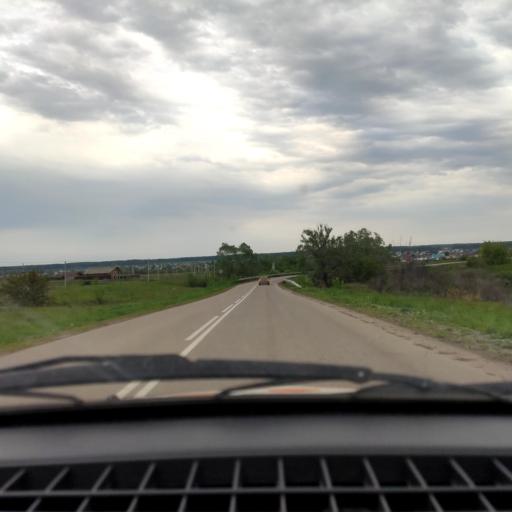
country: RU
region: Bashkortostan
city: Avdon
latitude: 54.5599
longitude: 55.7629
